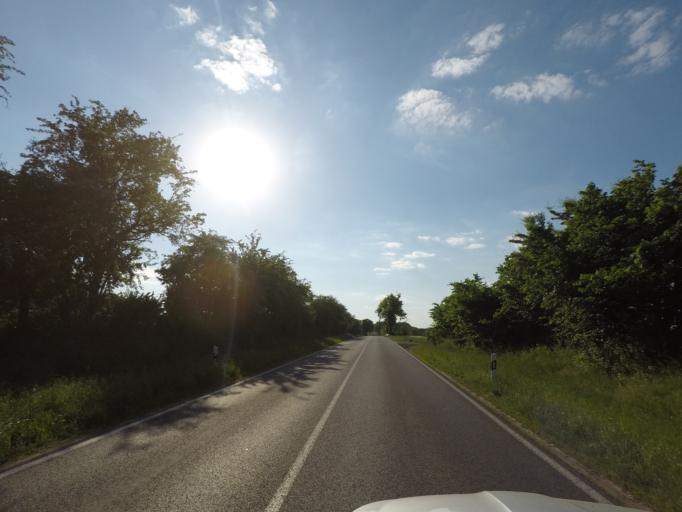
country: DE
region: Brandenburg
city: Falkenberg
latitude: 52.8052
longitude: 13.9405
